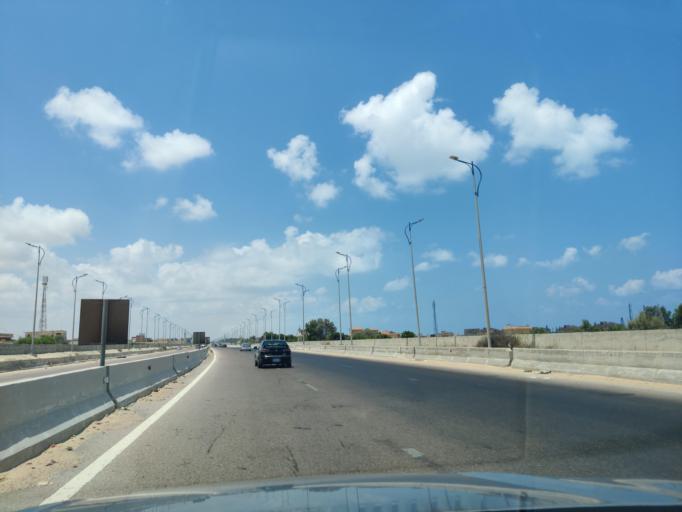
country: EG
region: Alexandria
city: Alexandria
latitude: 30.9592
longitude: 29.5399
